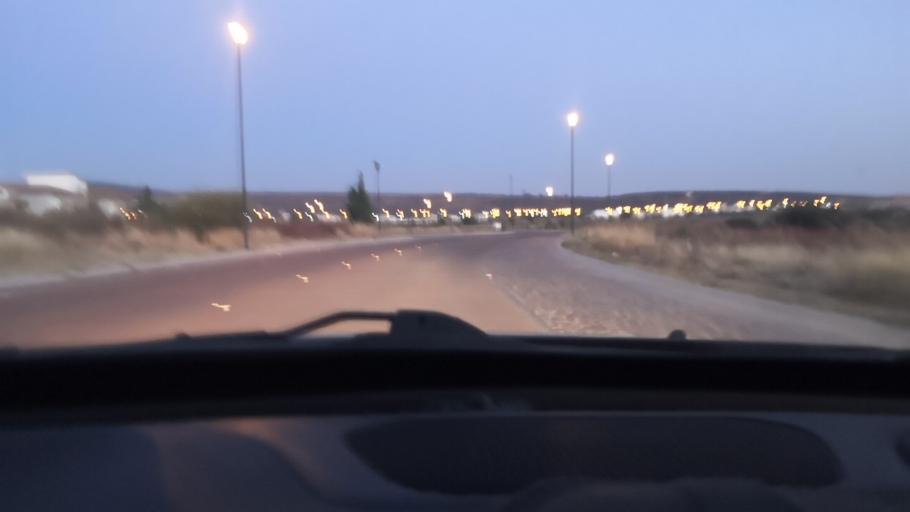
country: MX
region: Guanajuato
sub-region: Leon
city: Fraccionamiento Paseo de las Torres
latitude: 21.2325
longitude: -101.8006
